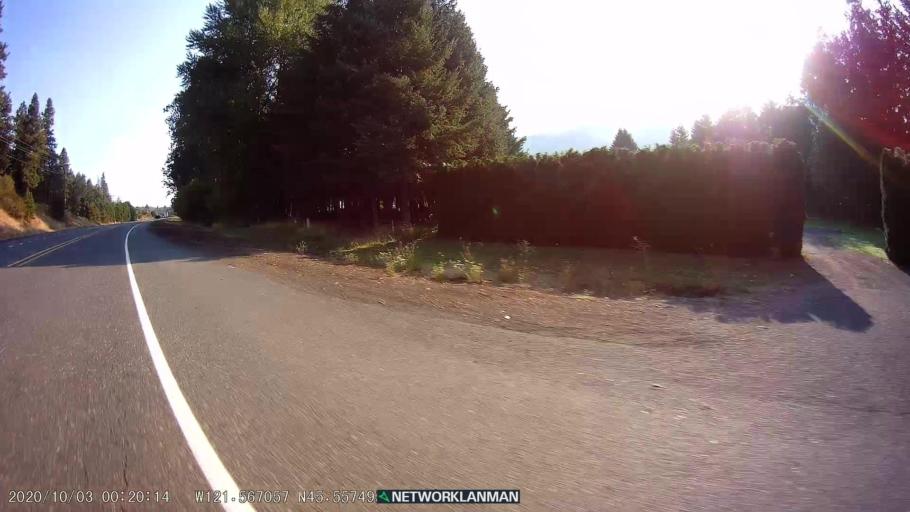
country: US
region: Oregon
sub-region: Hood River County
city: Odell
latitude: 45.5575
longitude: -121.5669
